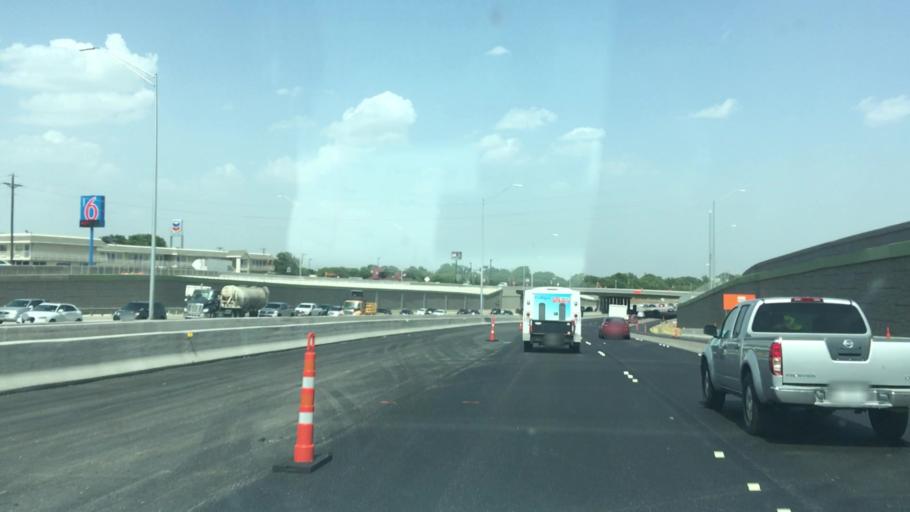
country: US
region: Texas
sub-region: Tarrant County
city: Euless
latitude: 32.8382
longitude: -97.0857
